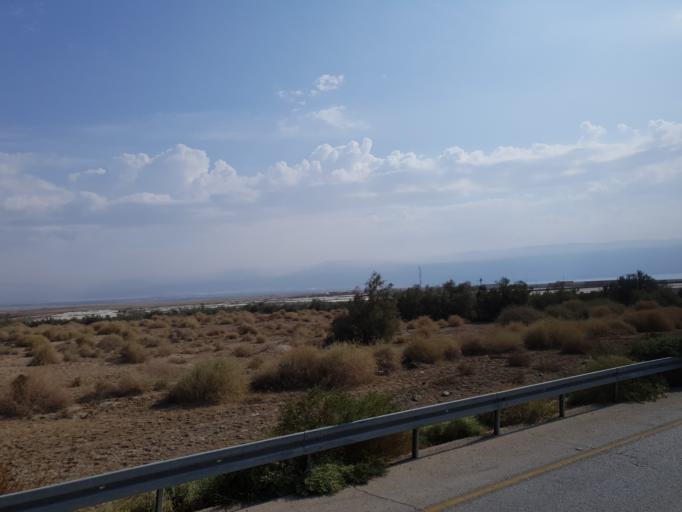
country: PS
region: West Bank
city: Jericho
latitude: 31.7777
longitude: 35.5037
